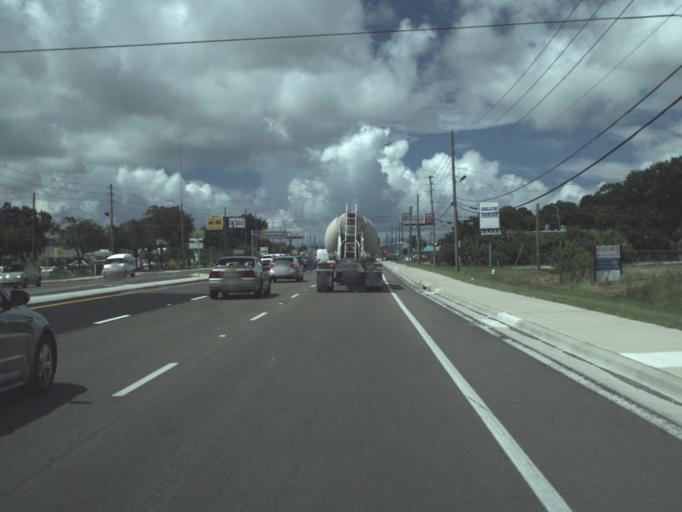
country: US
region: Florida
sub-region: Pinellas County
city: Largo
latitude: 27.8946
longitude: -82.7653
